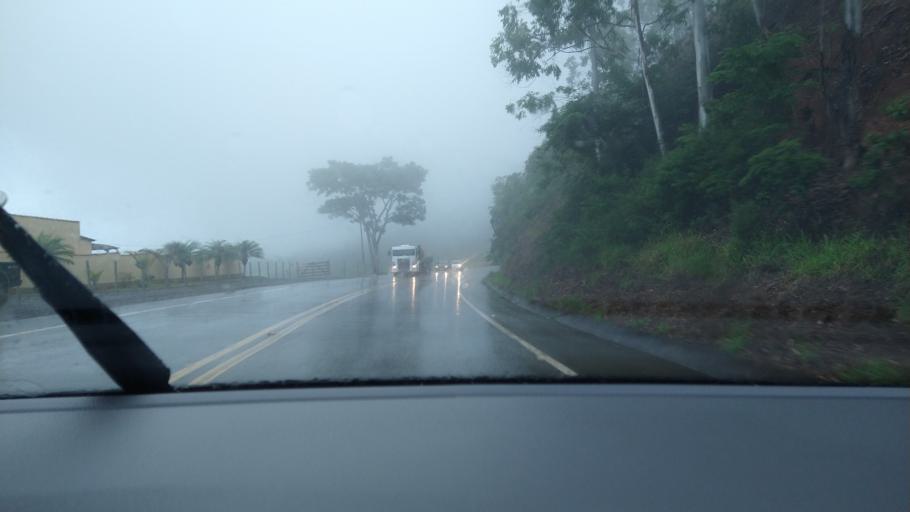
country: BR
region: Minas Gerais
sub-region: Ponte Nova
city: Ponte Nova
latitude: -20.5622
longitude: -42.8726
